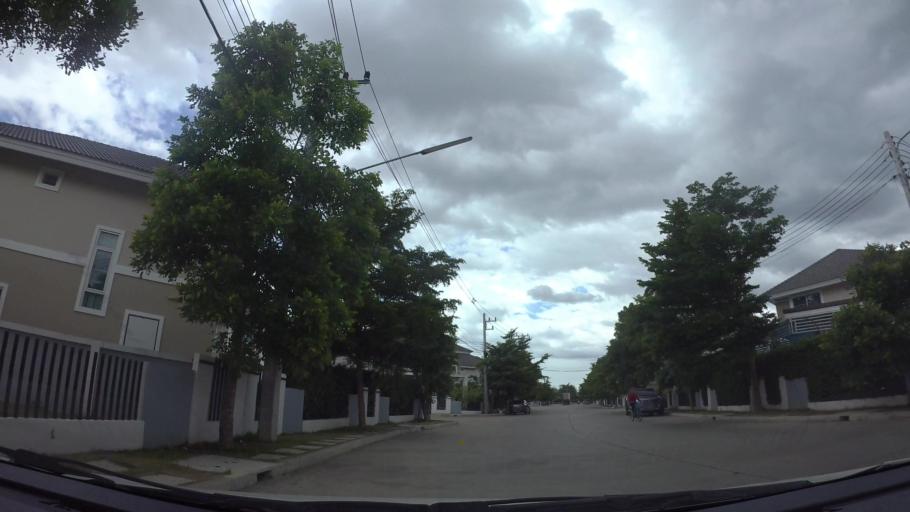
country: TH
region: Chiang Mai
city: Saraphi
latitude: 18.7480
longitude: 99.0430
